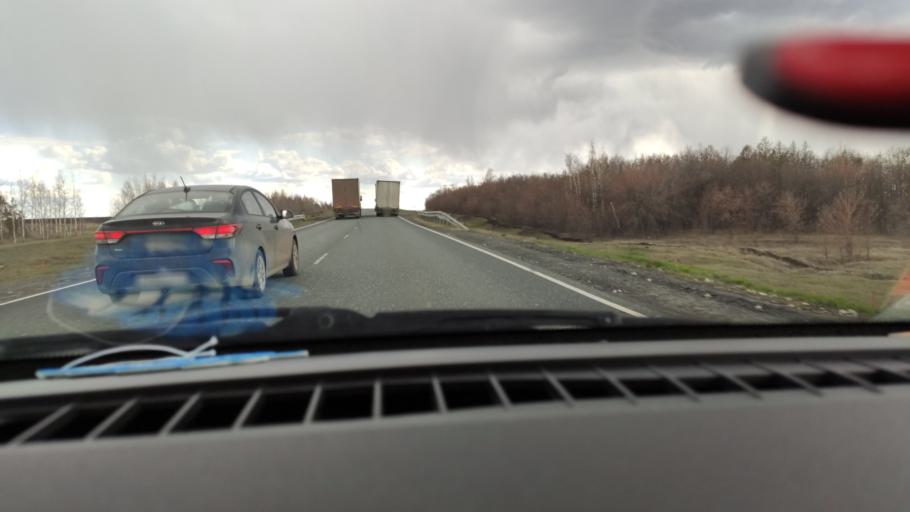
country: RU
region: Saratov
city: Balakovo
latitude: 52.1632
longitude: 47.8241
